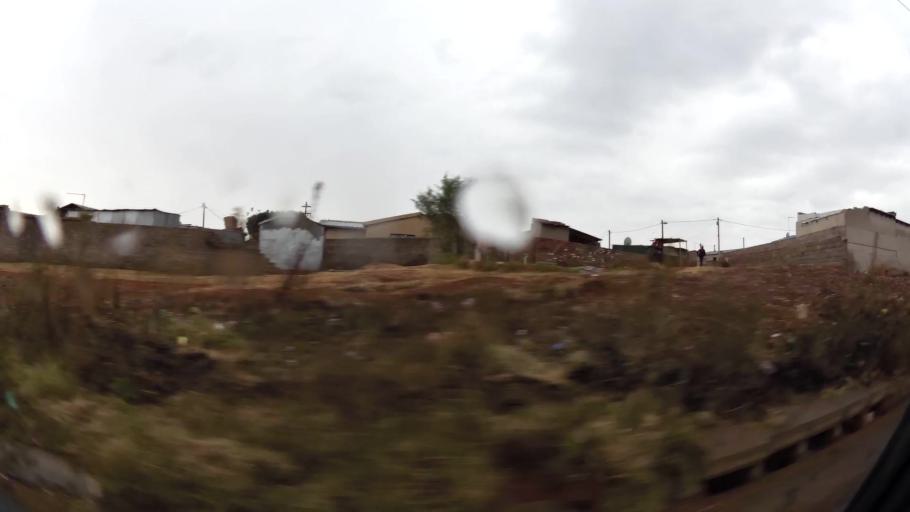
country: ZA
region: Gauteng
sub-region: West Rand District Municipality
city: Randfontein
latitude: -26.1754
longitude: 27.7788
